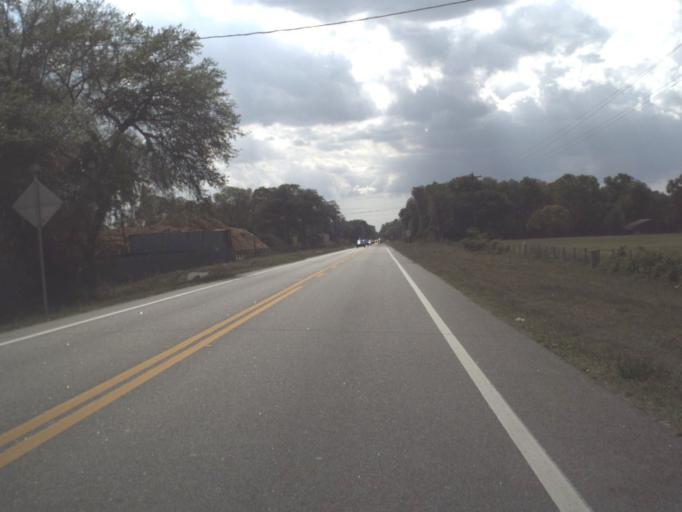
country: US
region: Florida
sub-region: Hernando County
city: Ridge Manor
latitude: 28.5552
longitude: -82.0576
